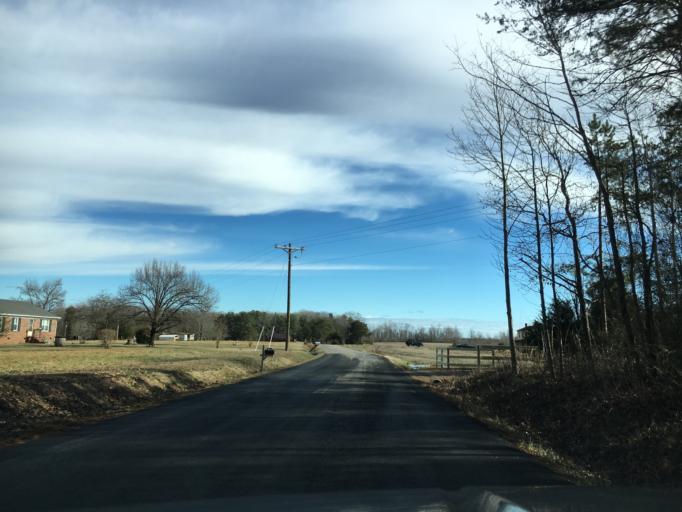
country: US
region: Virginia
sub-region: Nottoway County
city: Crewe
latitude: 37.3138
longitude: -78.1877
